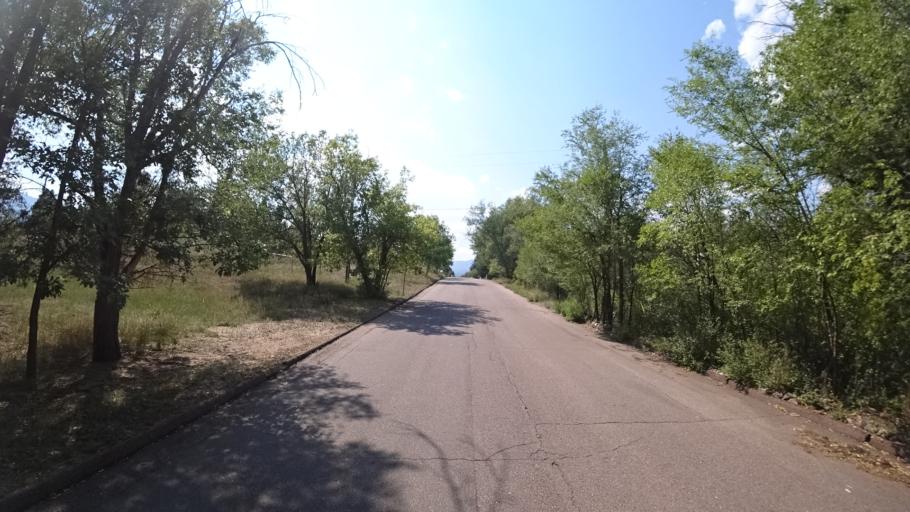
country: US
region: Colorado
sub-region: El Paso County
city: Colorado Springs
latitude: 38.8000
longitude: -104.8250
